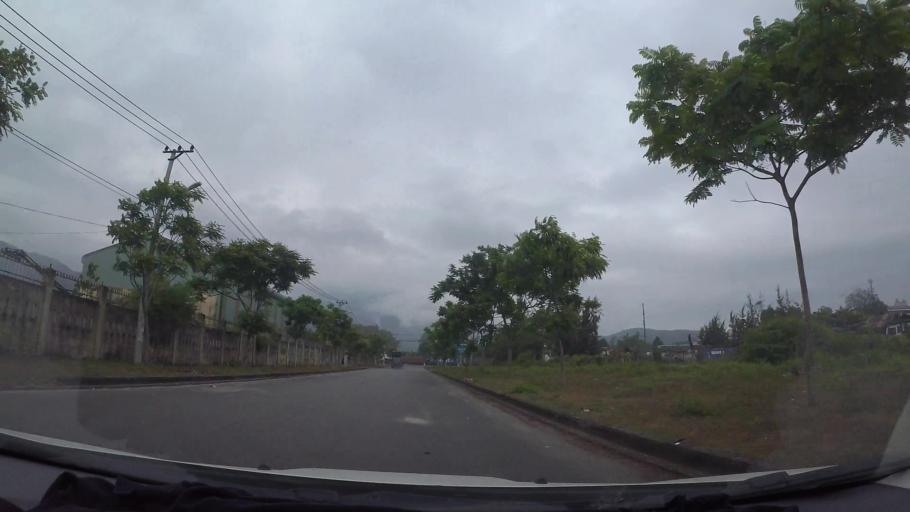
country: VN
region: Da Nang
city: Lien Chieu
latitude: 16.1266
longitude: 108.1173
